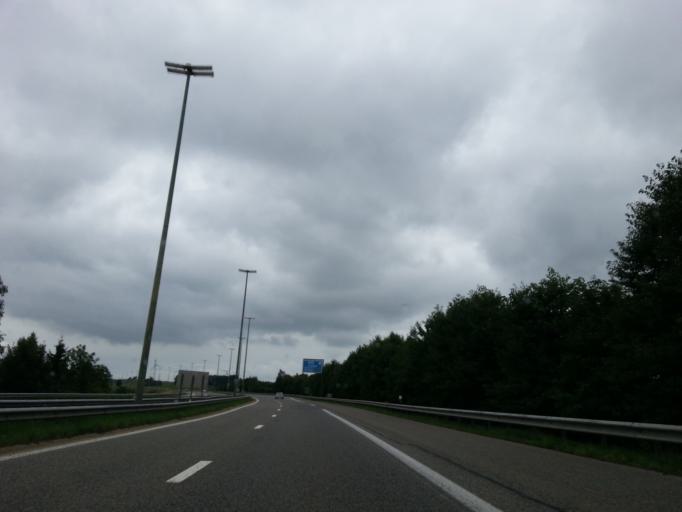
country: BE
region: Wallonia
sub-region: Province de Liege
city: Saint-Vith
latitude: 50.2846
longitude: 6.1067
